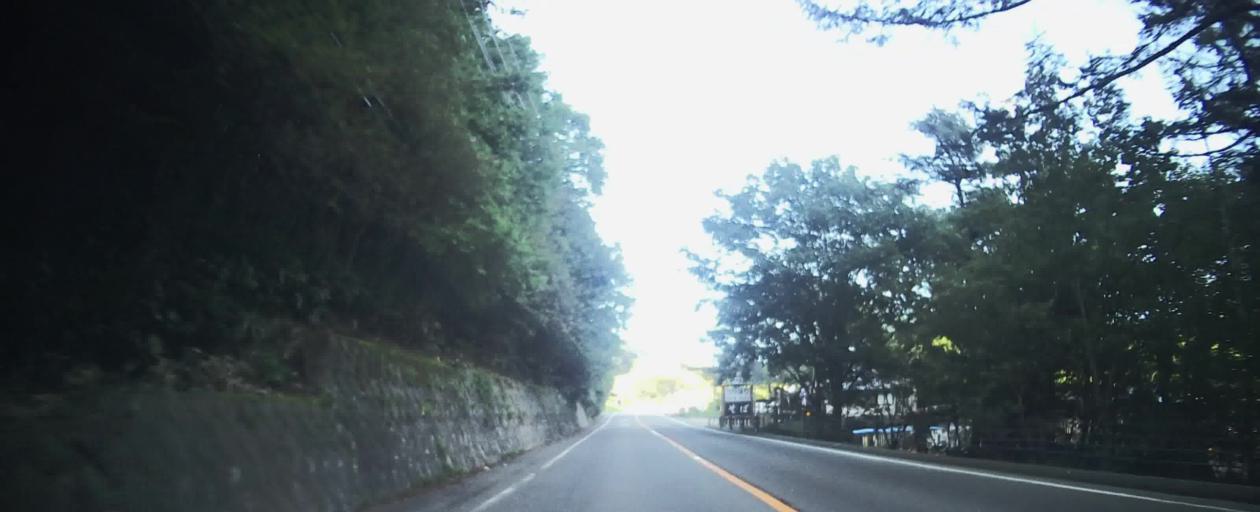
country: JP
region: Nagano
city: Nakano
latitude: 36.6249
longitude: 138.5853
